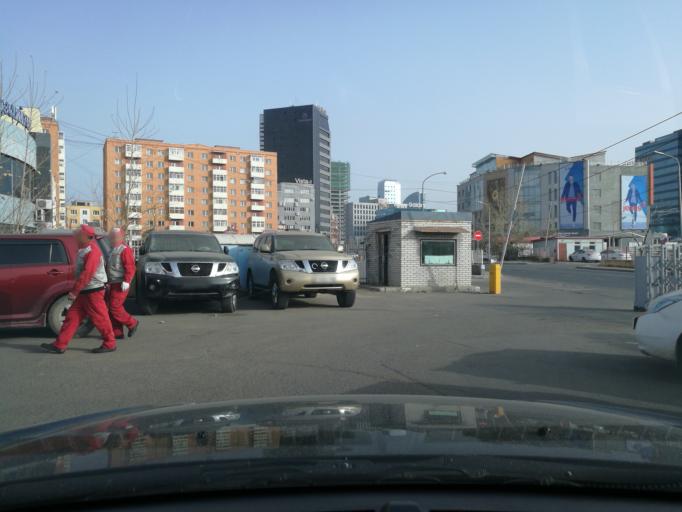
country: MN
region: Ulaanbaatar
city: Ulaanbaatar
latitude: 47.9087
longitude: 106.9117
